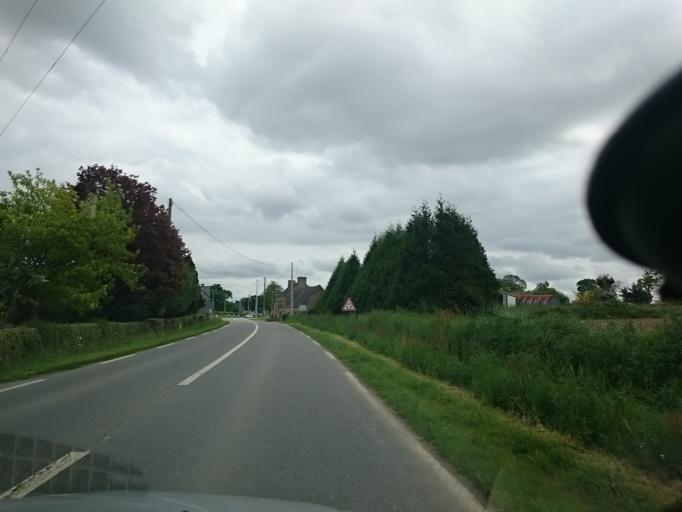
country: FR
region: Brittany
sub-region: Departement d'Ille-et-Vilaine
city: Antrain
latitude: 48.4522
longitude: -1.4777
